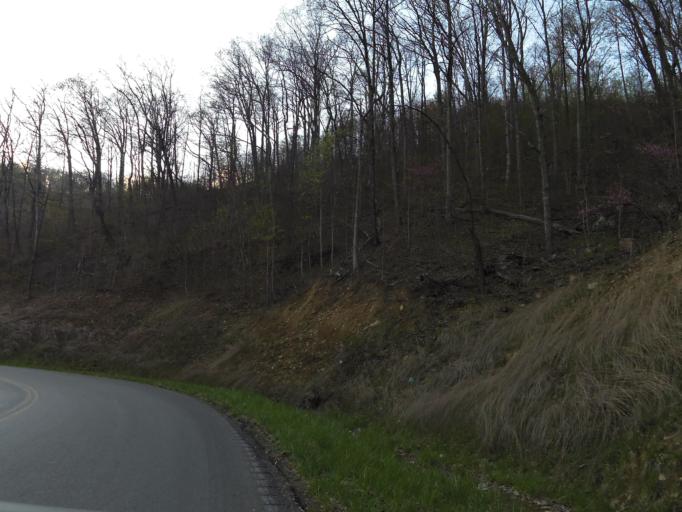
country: US
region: Kentucky
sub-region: Bell County
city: Middlesboro
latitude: 36.6237
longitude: -83.8667
